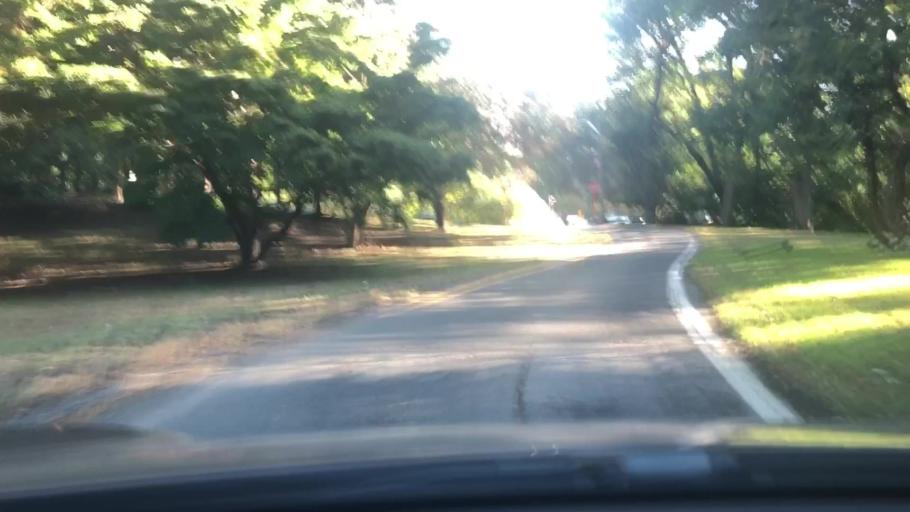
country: US
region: New York
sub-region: Westchester County
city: Bronxville
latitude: 40.9433
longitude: -73.8383
